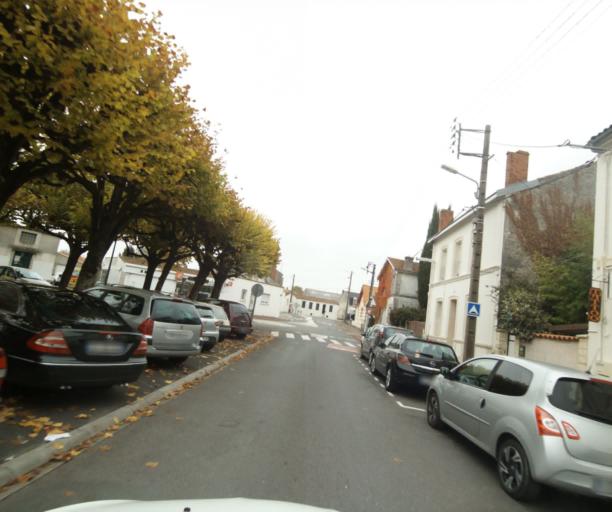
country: FR
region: Poitou-Charentes
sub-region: Departement de la Charente-Maritime
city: Saintes
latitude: 45.7479
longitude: -0.6219
